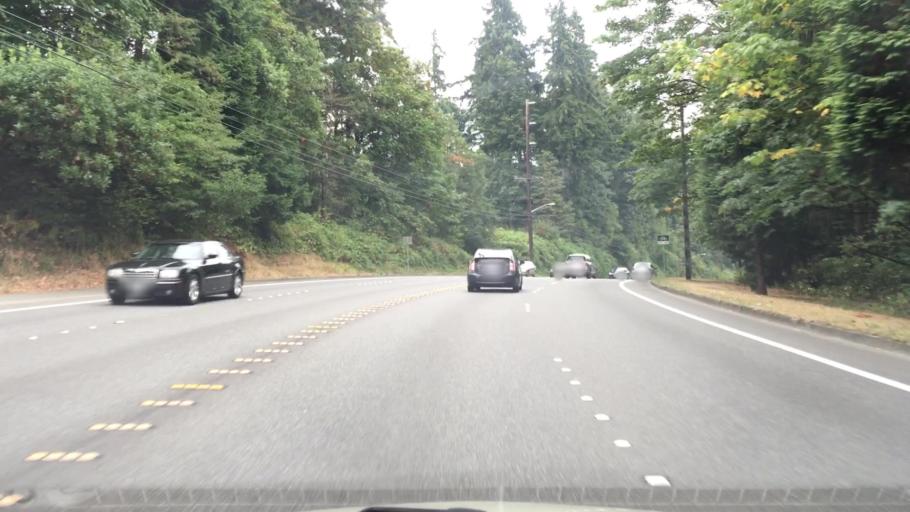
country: US
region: Washington
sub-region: King County
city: Newport
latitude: 47.5625
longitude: -122.1696
